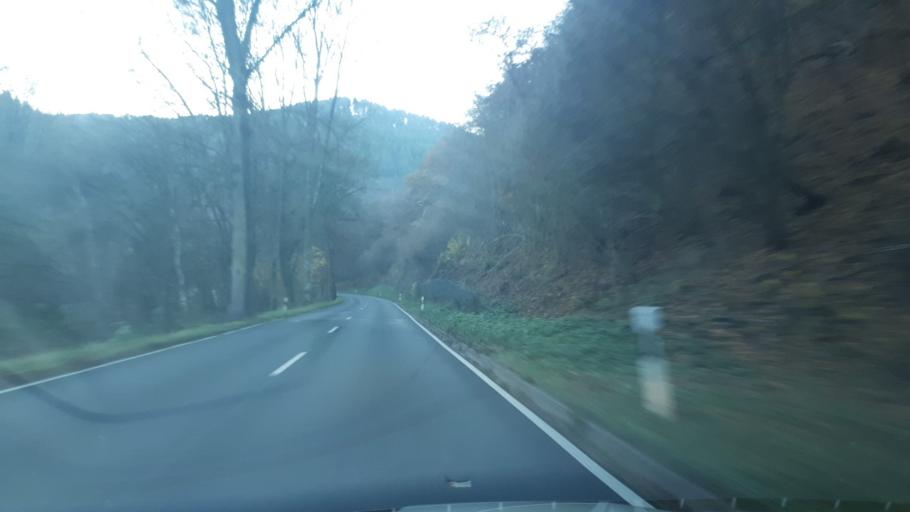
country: DE
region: Rheinland-Pfalz
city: Beuren
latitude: 50.0667
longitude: 7.0768
